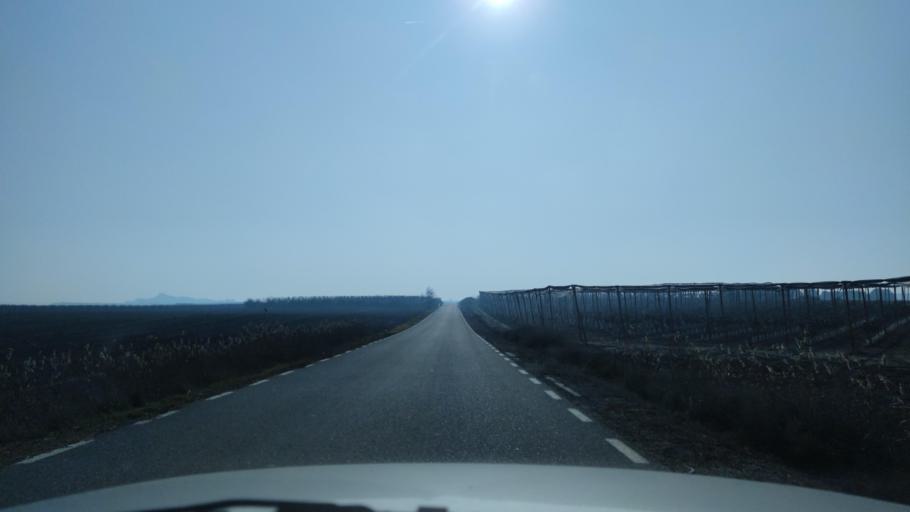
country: ES
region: Catalonia
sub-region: Provincia de Lleida
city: Sunyer
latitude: 41.5417
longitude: 0.5761
